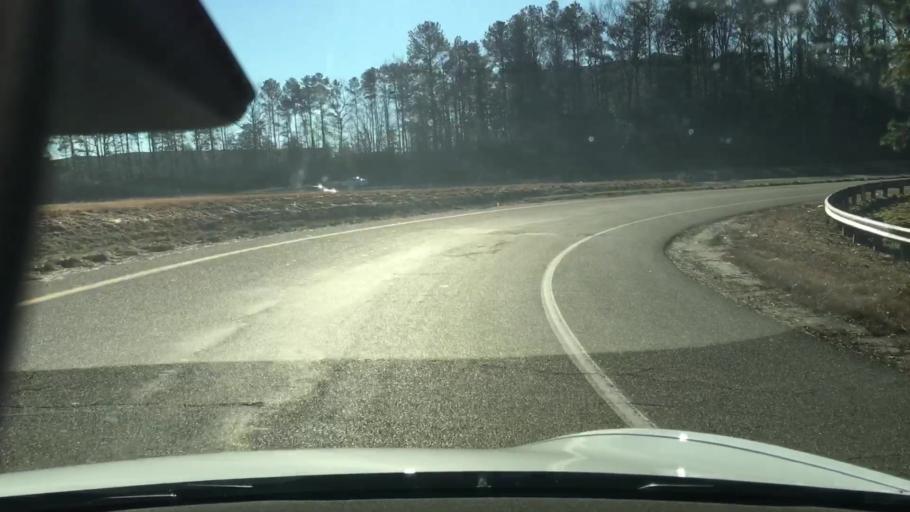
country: US
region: Virginia
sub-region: Henrico County
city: Montrose
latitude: 37.5331
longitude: -77.3603
